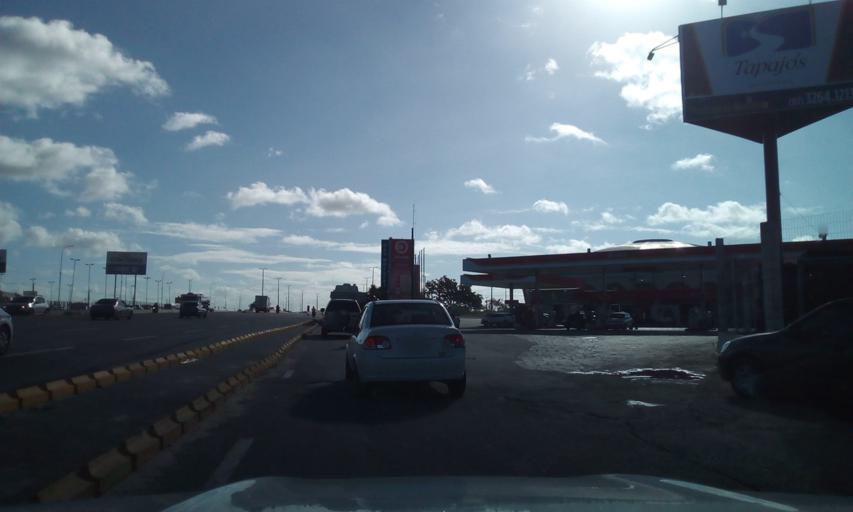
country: BR
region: Paraiba
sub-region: Joao Pessoa
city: Joao Pessoa
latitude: -7.1706
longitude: -34.8689
